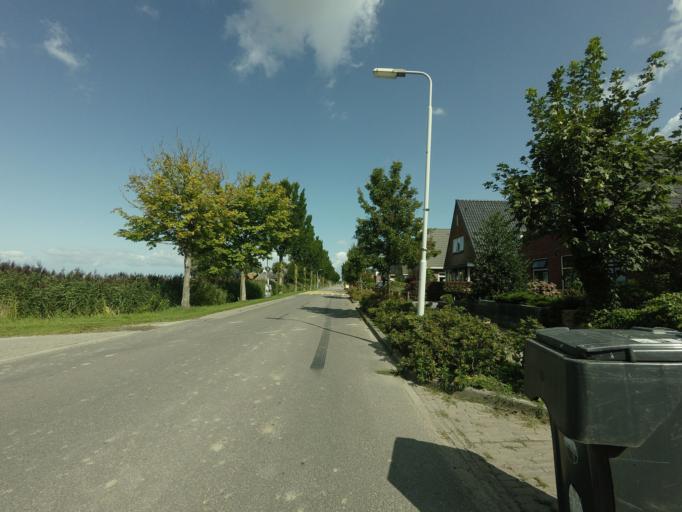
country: NL
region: Friesland
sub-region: Gemeente Het Bildt
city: Sint Annaparochie
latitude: 53.2815
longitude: 5.6561
